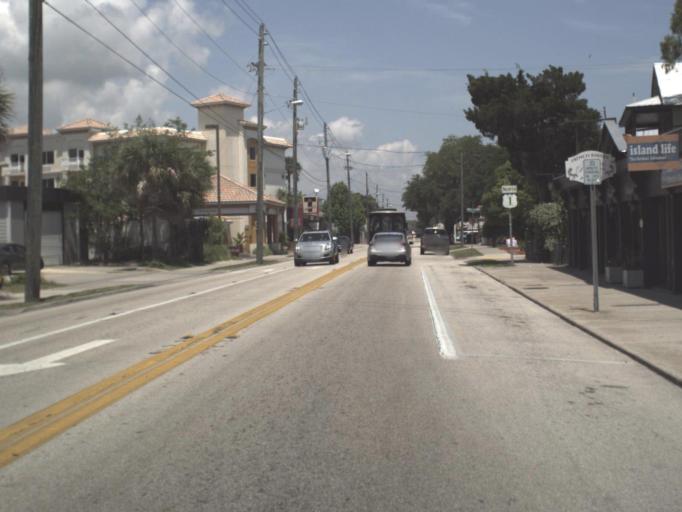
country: US
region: Florida
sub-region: Saint Johns County
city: Saint Augustine
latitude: 29.9001
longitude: -81.3149
